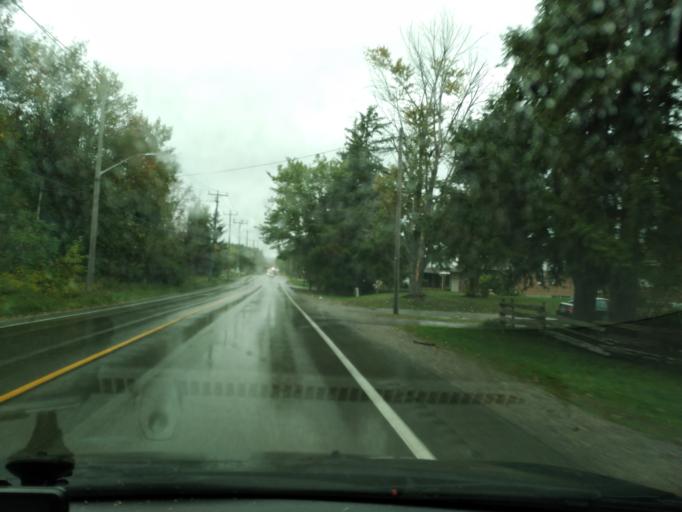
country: CA
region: Ontario
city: Barrie
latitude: 44.3616
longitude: -79.6677
